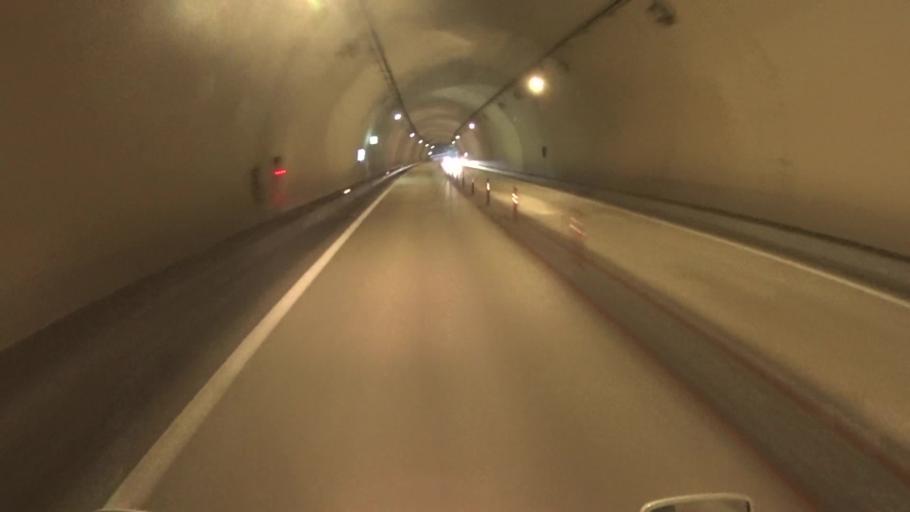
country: JP
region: Kyoto
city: Miyazu
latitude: 35.5453
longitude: 135.1531
